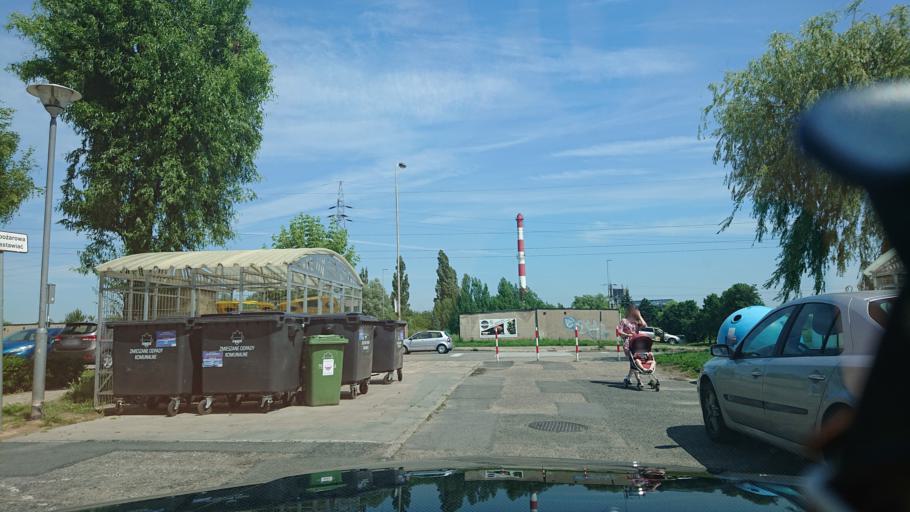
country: PL
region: Greater Poland Voivodeship
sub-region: Powiat gnieznienski
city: Gniezno
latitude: 52.5513
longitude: 17.6115
